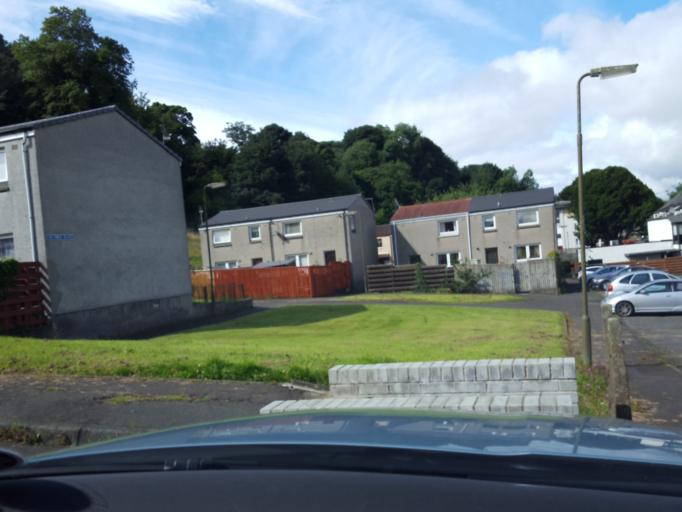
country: GB
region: Scotland
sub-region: Falkirk
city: Bo'ness
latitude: 56.0158
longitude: -3.5933
